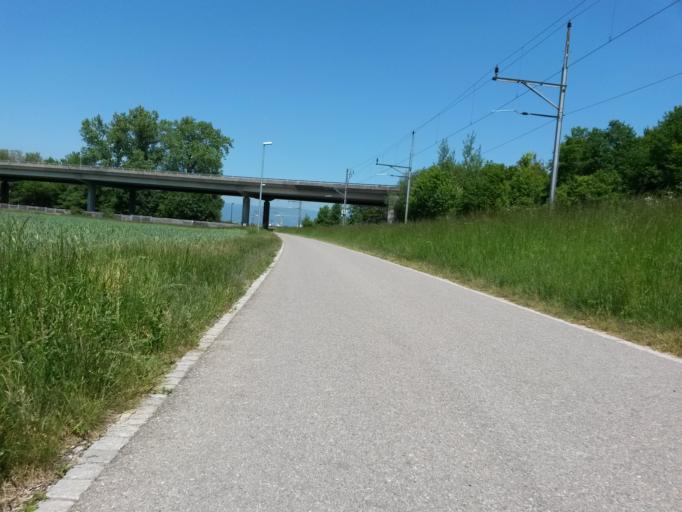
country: CH
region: Bern
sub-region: Seeland District
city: Lyss
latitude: 47.0606
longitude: 7.2946
